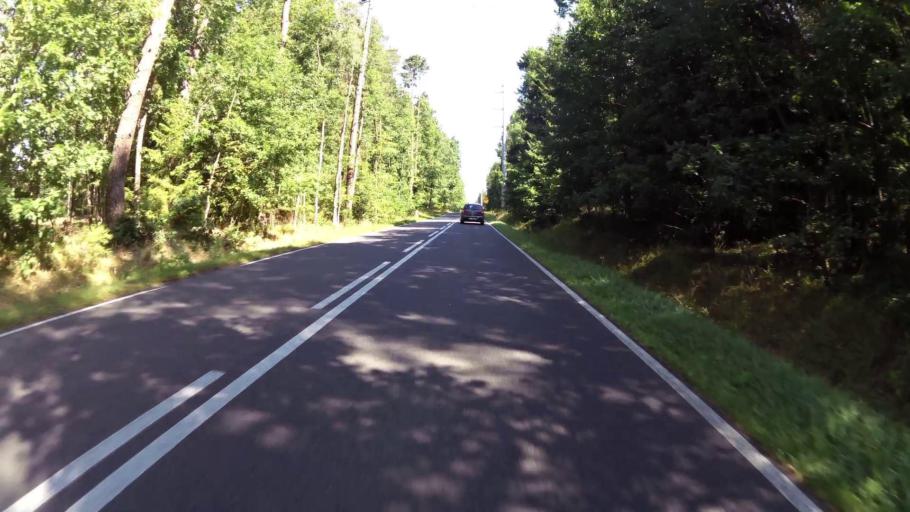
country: PL
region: West Pomeranian Voivodeship
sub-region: Powiat drawski
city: Wierzchowo
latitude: 53.4457
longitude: 16.2114
